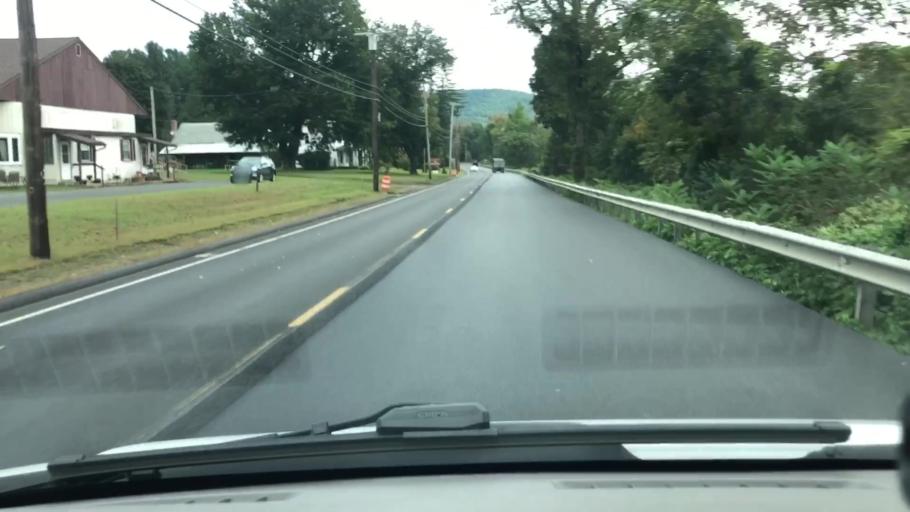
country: US
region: Massachusetts
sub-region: Franklin County
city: Buckland
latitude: 42.6185
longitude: -72.7965
